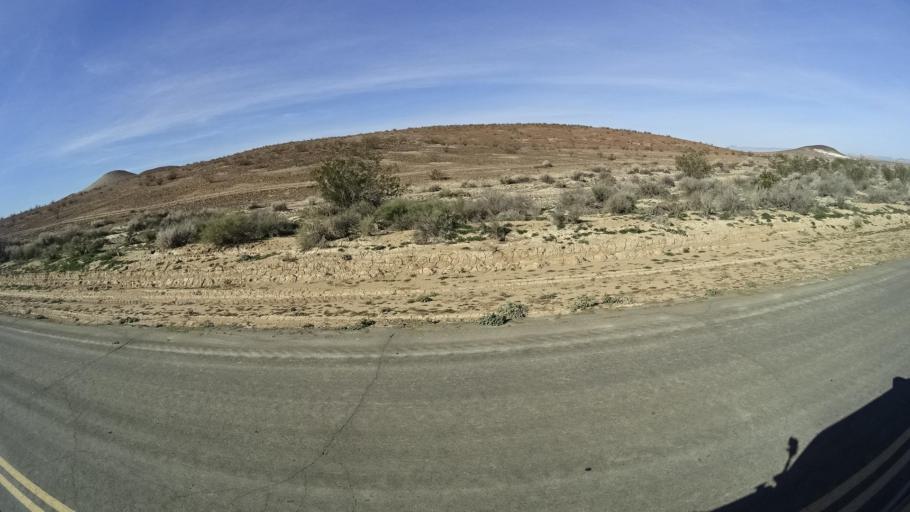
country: US
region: California
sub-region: Kern County
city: North Edwards
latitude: 35.0614
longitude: -117.8066
